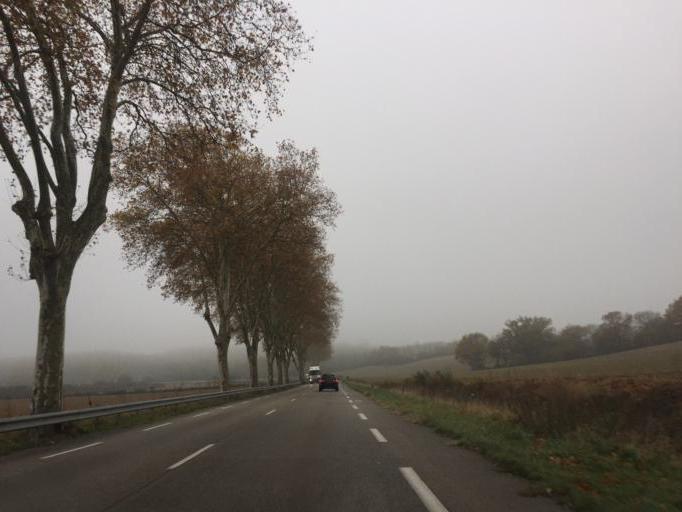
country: FR
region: Rhone-Alpes
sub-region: Departement de l'Ain
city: Mionnay
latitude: 45.8852
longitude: 4.9170
